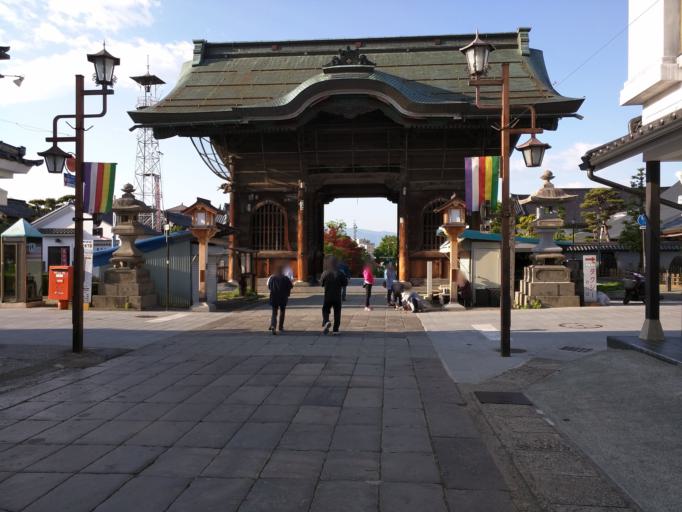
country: JP
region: Nagano
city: Nagano-shi
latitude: 36.6588
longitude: 138.1876
